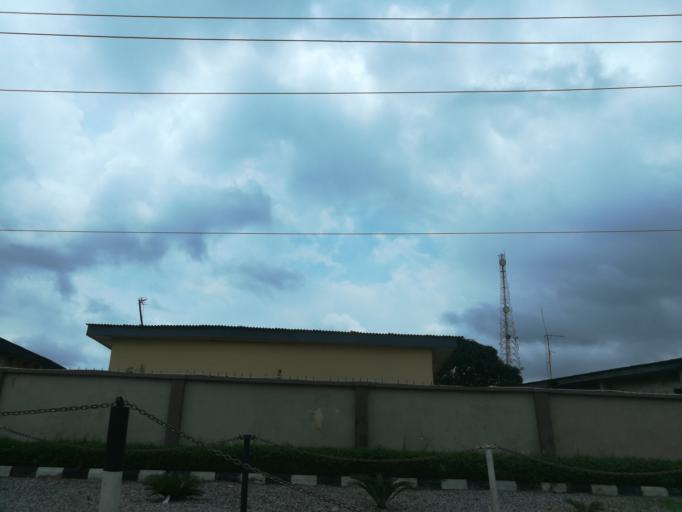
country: NG
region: Lagos
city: Ikeja
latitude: 6.5897
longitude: 3.3454
